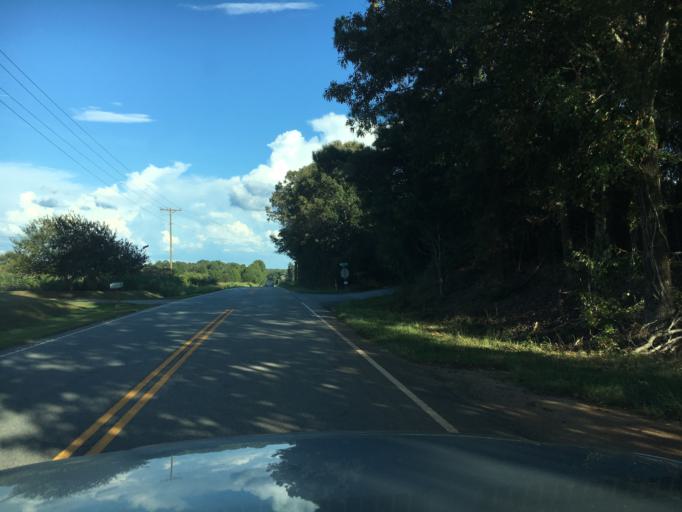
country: US
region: South Carolina
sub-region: Greenville County
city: Five Forks
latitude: 34.7965
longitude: -82.1449
